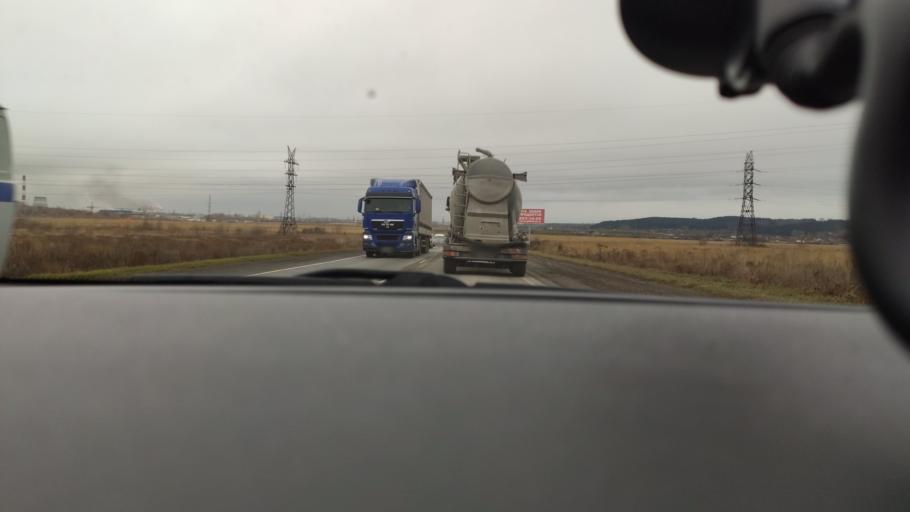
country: RU
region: Perm
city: Froly
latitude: 57.9181
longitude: 56.1833
